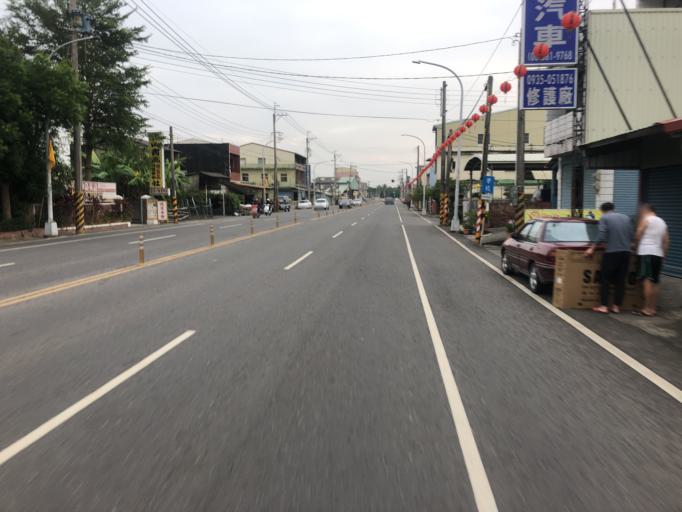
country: TW
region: Taiwan
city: Xinying
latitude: 23.1508
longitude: 120.2874
